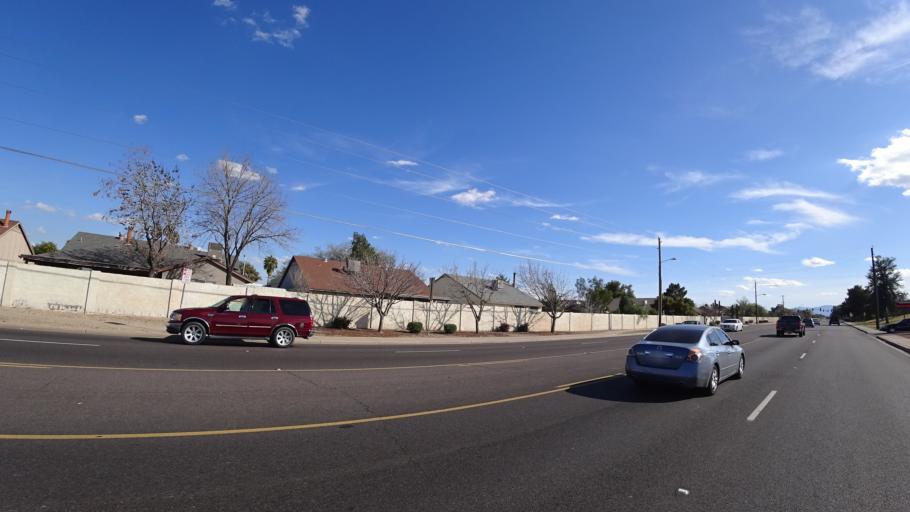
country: US
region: Arizona
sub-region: Maricopa County
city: Glendale
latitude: 33.5332
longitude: -112.2206
